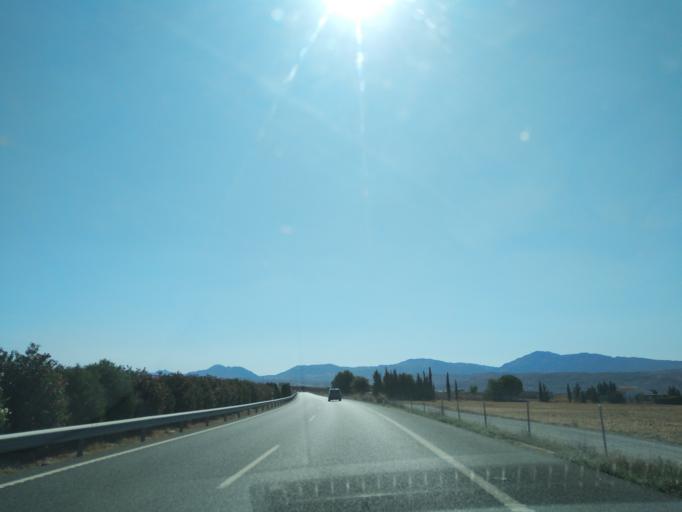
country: ES
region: Andalusia
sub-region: Provincia de Malaga
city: Mollina
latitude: 37.0890
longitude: -4.6250
